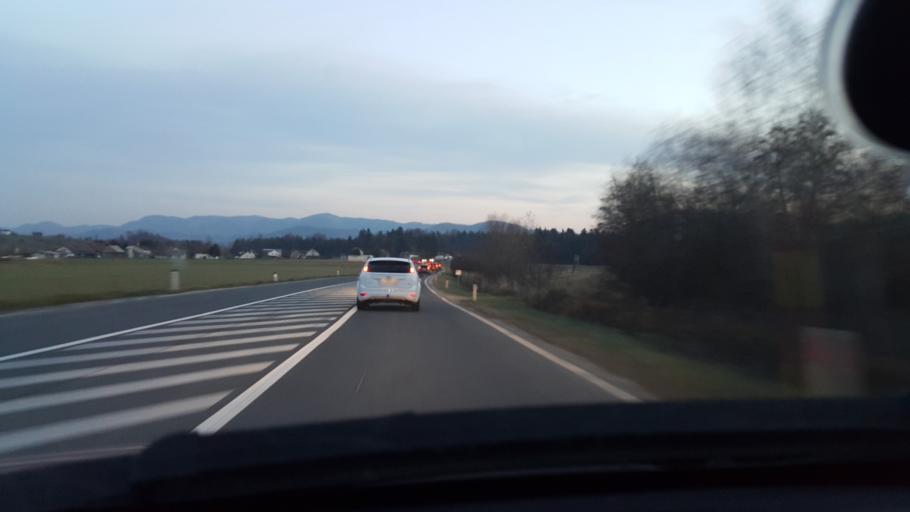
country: SI
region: Zalec
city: Zalec
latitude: 46.2763
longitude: 15.1867
